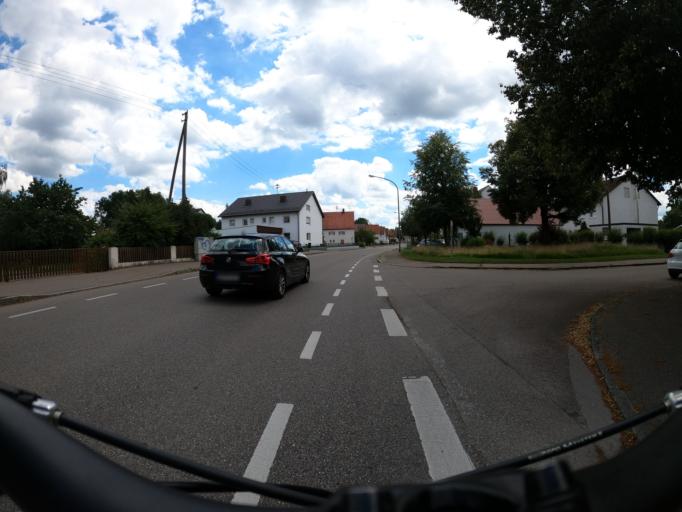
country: DE
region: Bavaria
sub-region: Swabia
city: Nersingen
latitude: 48.4173
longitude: 10.1351
